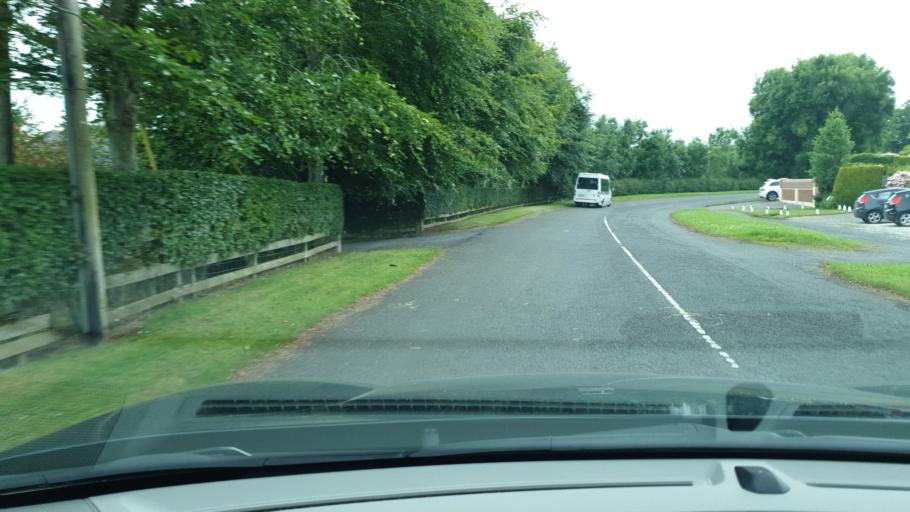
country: IE
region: Leinster
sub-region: An Mhi
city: Dunboyne
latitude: 53.4388
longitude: -6.4717
